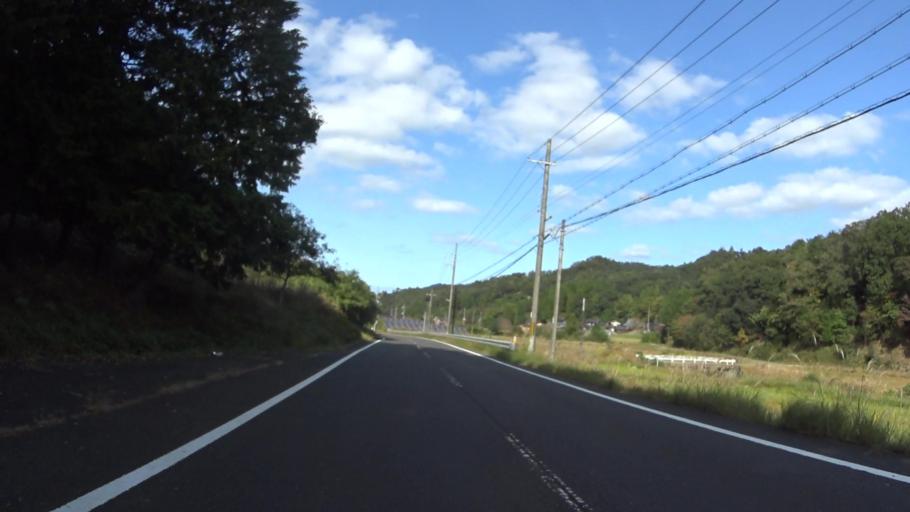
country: JP
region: Hyogo
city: Toyooka
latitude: 35.5590
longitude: 134.9797
